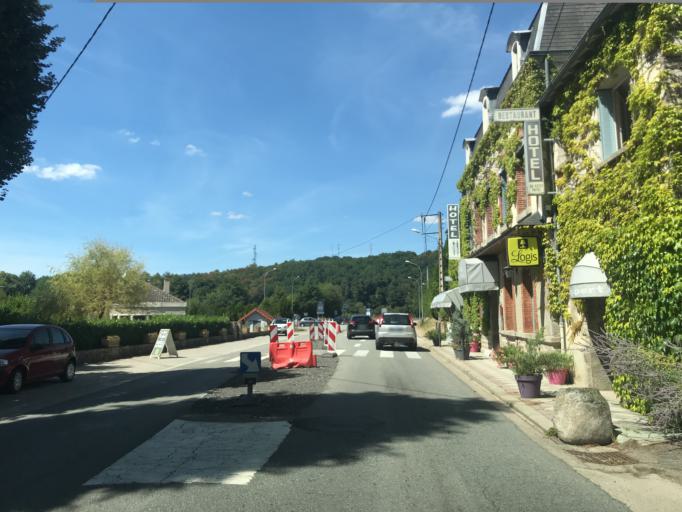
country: FR
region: Limousin
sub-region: Departement de la Creuse
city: Aubusson
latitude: 45.9247
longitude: 2.1908
